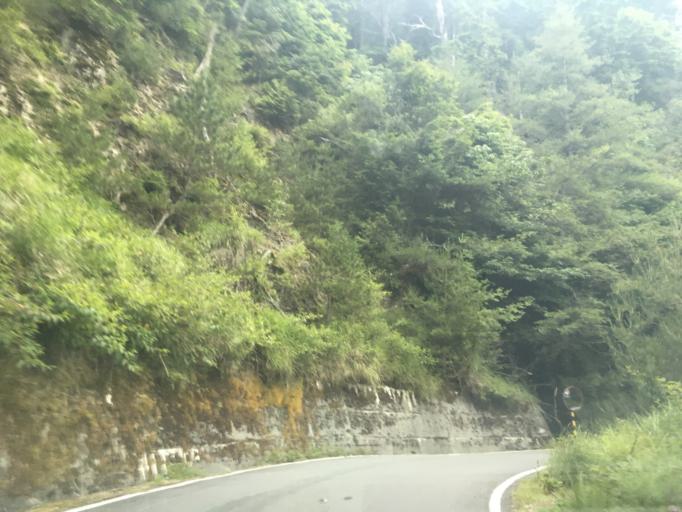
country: TW
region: Taiwan
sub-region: Nantou
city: Puli
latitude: 24.2742
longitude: 121.0296
